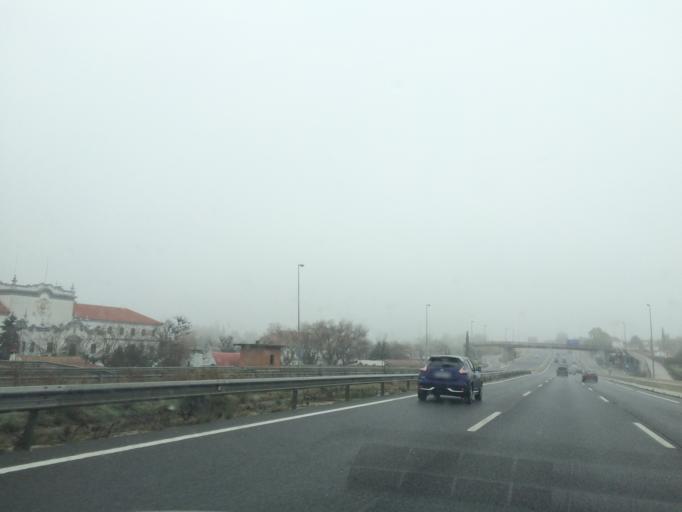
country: ES
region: Madrid
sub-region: Provincia de Madrid
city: Tres Cantos
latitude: 40.5574
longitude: -3.7116
